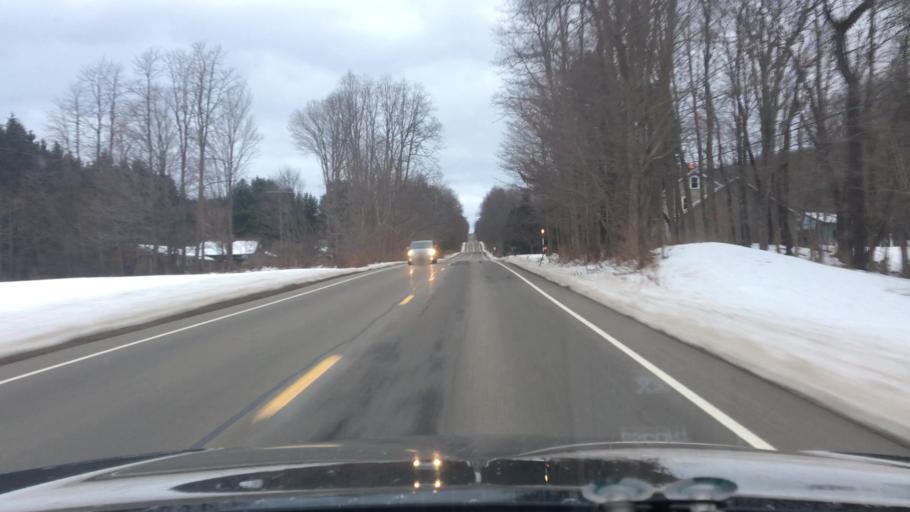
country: US
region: New York
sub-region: Chautauqua County
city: Lakewood
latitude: 42.1748
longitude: -79.3694
